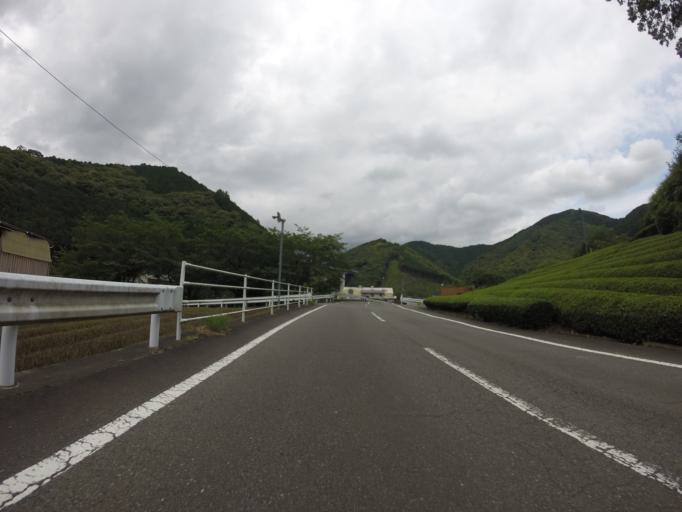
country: JP
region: Shizuoka
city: Shizuoka-shi
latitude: 35.0034
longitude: 138.3135
